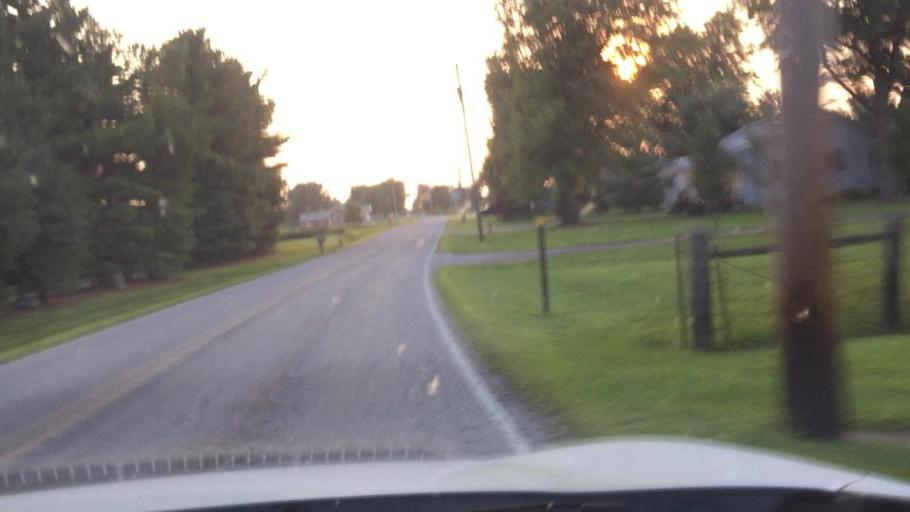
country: US
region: Ohio
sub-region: Madison County
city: Choctaw Lake
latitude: 39.9465
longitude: -83.5294
